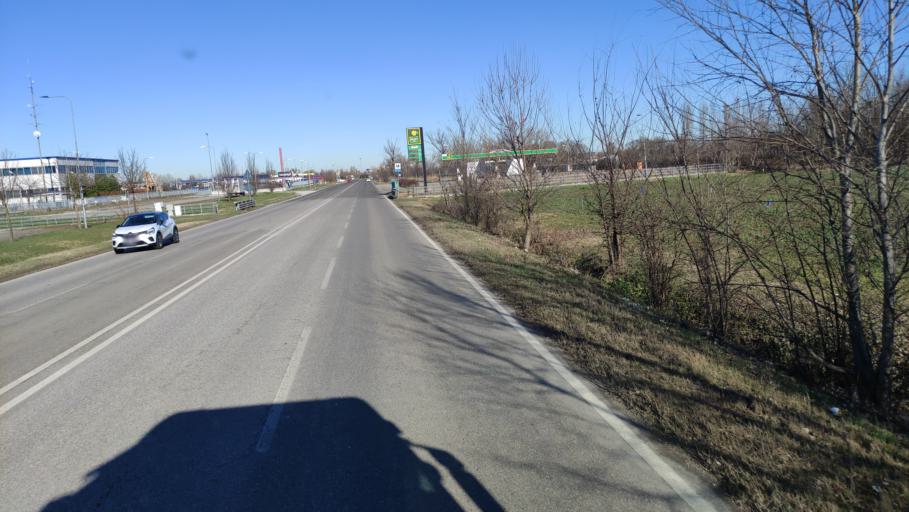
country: IT
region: Emilia-Romagna
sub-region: Provincia di Reggio Emilia
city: Correggio
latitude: 44.7535
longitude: 10.7889
